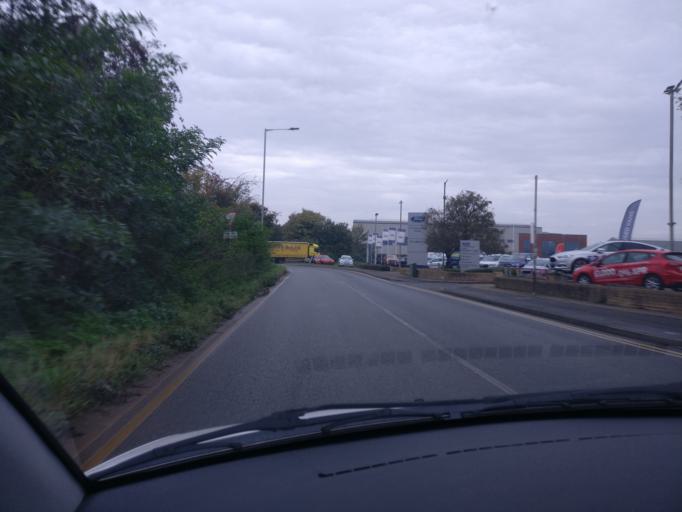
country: GB
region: England
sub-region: Peterborough
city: Eye
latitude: 52.5892
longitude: -0.2023
